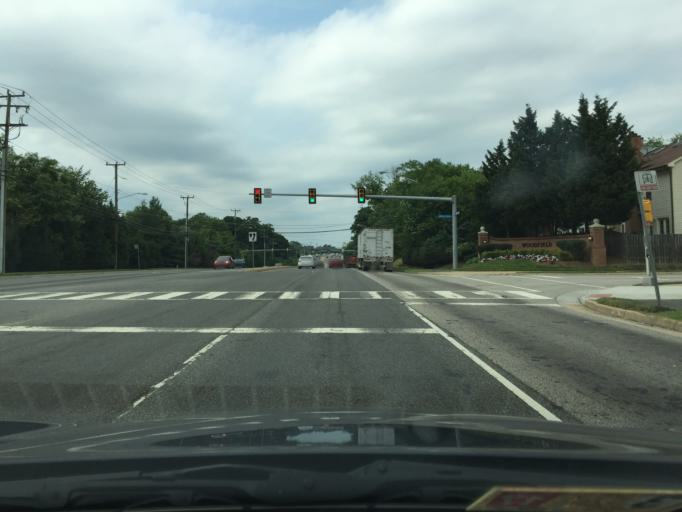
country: US
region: Virginia
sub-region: Fairfax County
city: Franconia
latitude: 38.7864
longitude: -77.1363
